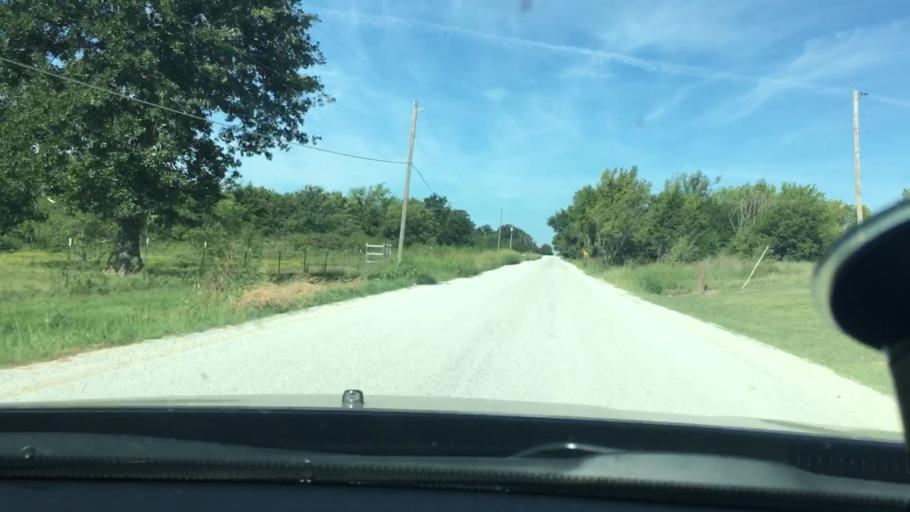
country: US
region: Oklahoma
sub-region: Carter County
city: Lone Grove
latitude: 34.2165
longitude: -97.2491
